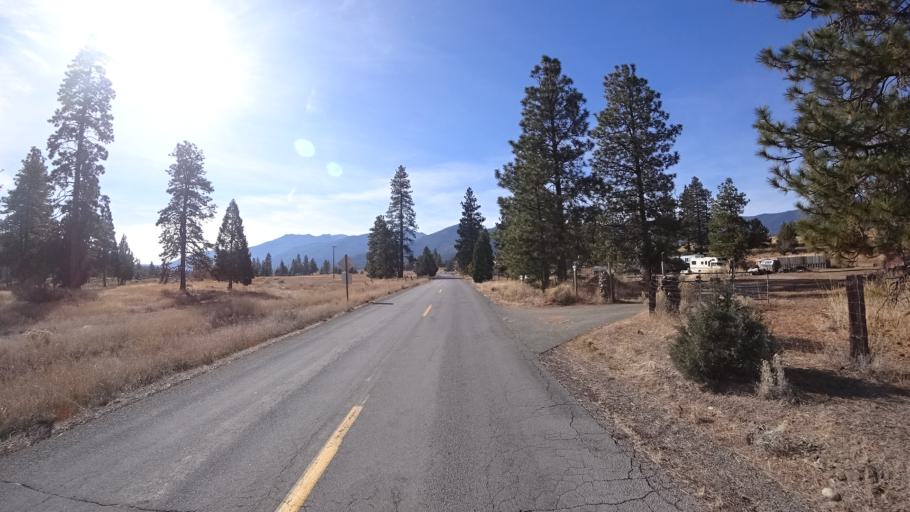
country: US
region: California
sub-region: Siskiyou County
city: Weed
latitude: 41.4463
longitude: -122.4335
